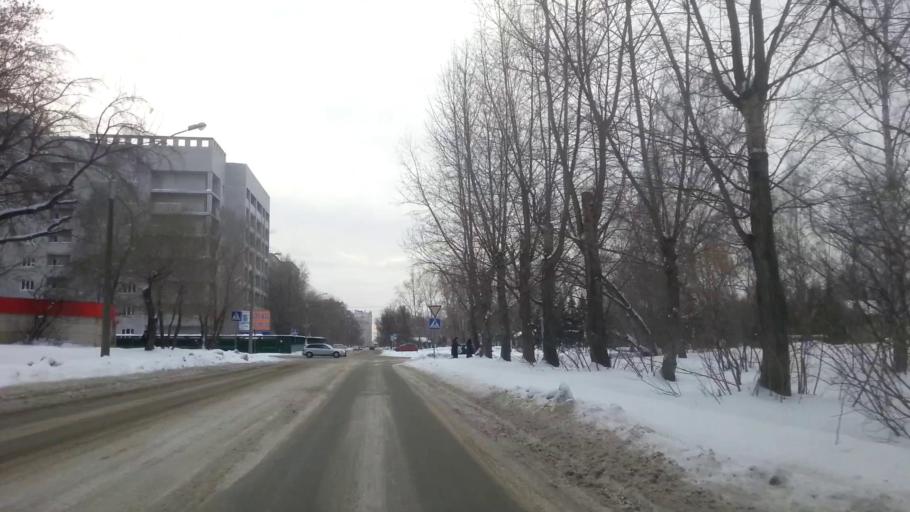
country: RU
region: Altai Krai
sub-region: Gorod Barnaulskiy
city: Barnaul
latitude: 53.3660
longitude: 83.6929
